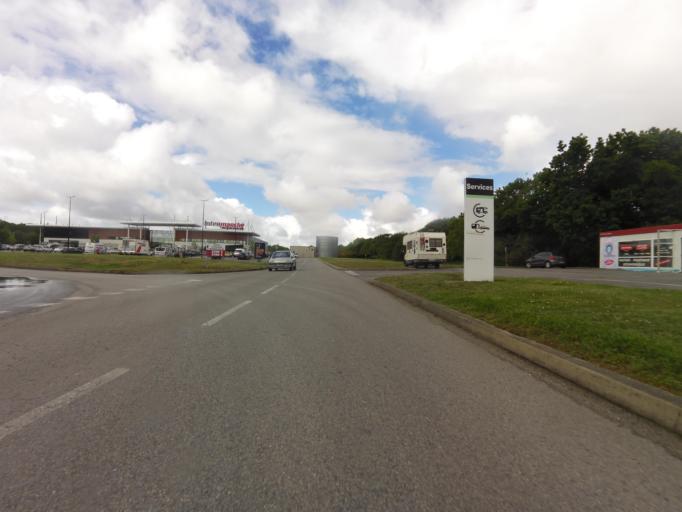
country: FR
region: Brittany
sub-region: Departement du Morbihan
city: Crach
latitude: 47.6041
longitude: -2.9963
